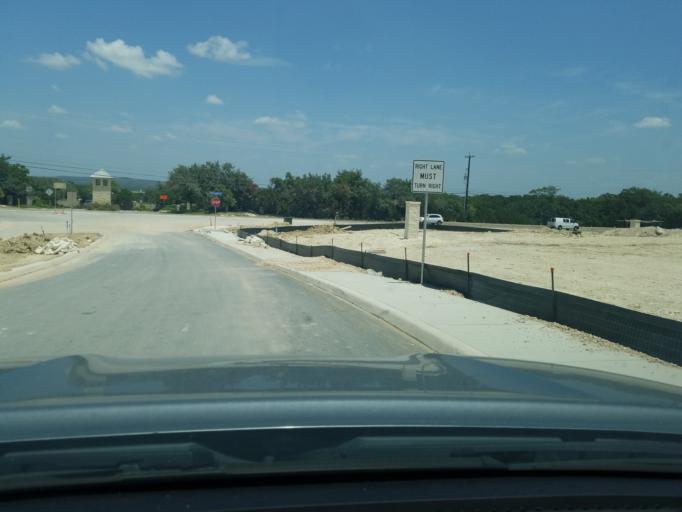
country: US
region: Texas
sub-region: Bexar County
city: Timberwood Park
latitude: 29.7076
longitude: -98.4993
